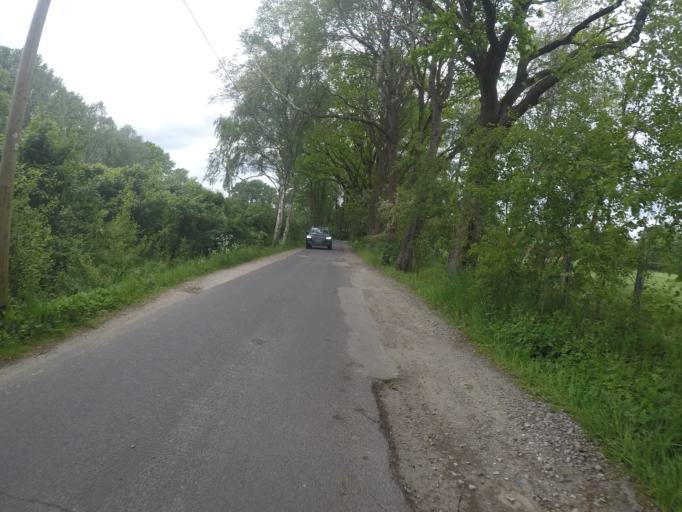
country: DE
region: Schleswig-Holstein
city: Bonningstedt
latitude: 53.6538
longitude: 9.9398
